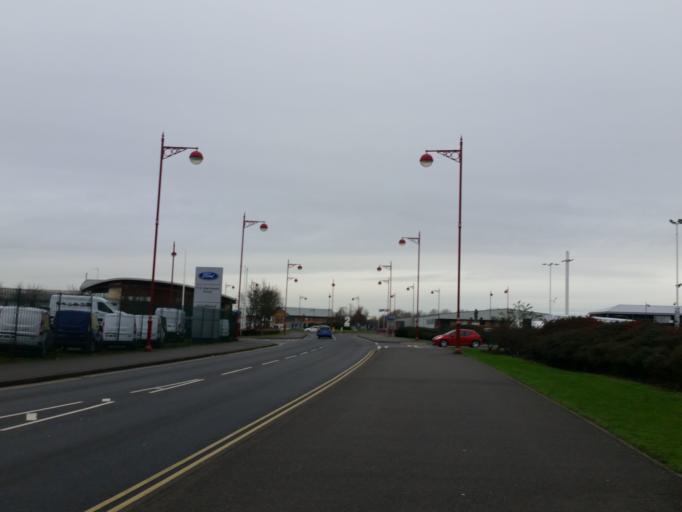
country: GB
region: England
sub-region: Derby
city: Derby
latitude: 52.9137
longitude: -1.4486
